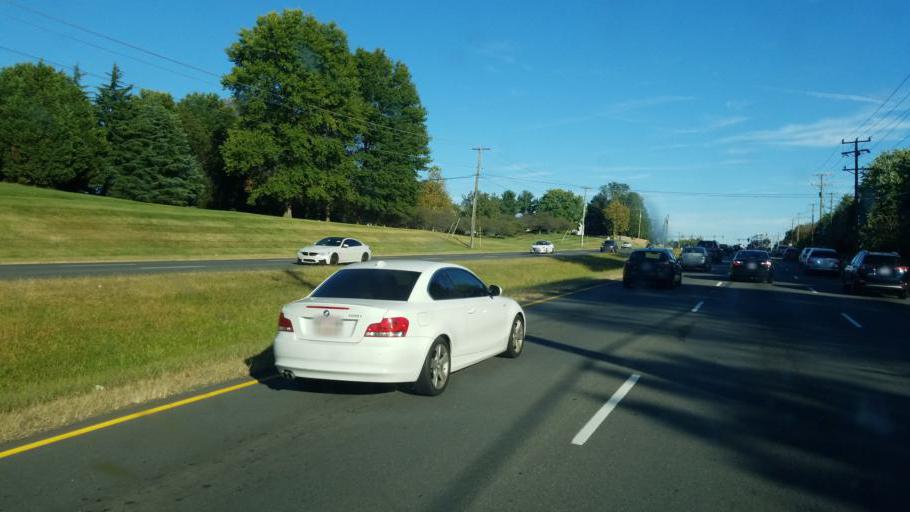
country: US
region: Virginia
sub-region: Fairfax County
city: Greenbriar
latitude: 38.8855
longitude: -77.4093
